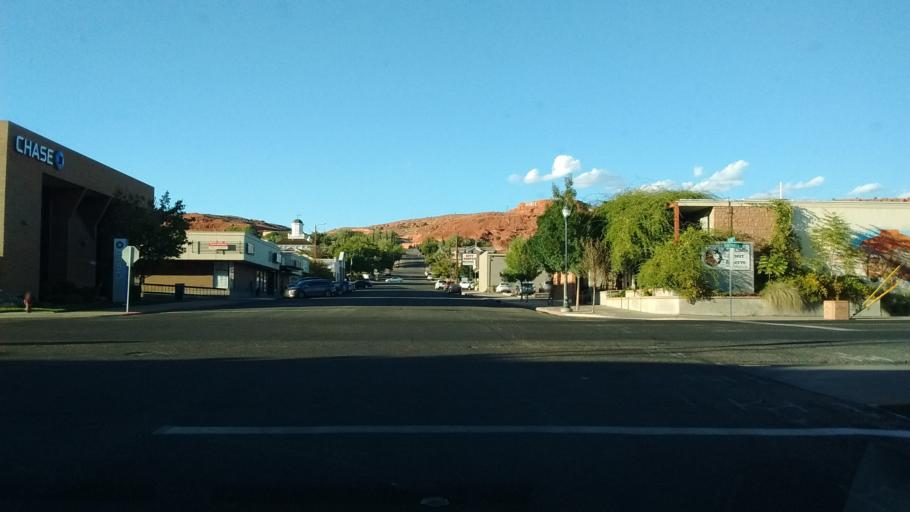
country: US
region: Utah
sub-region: Washington County
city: Saint George
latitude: 37.1080
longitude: -113.5811
